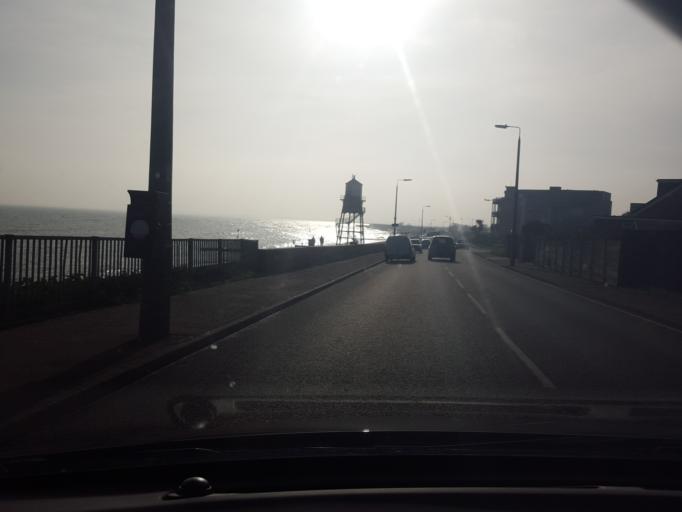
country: GB
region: England
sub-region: Essex
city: Dovercourt
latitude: 51.9316
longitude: 1.2765
